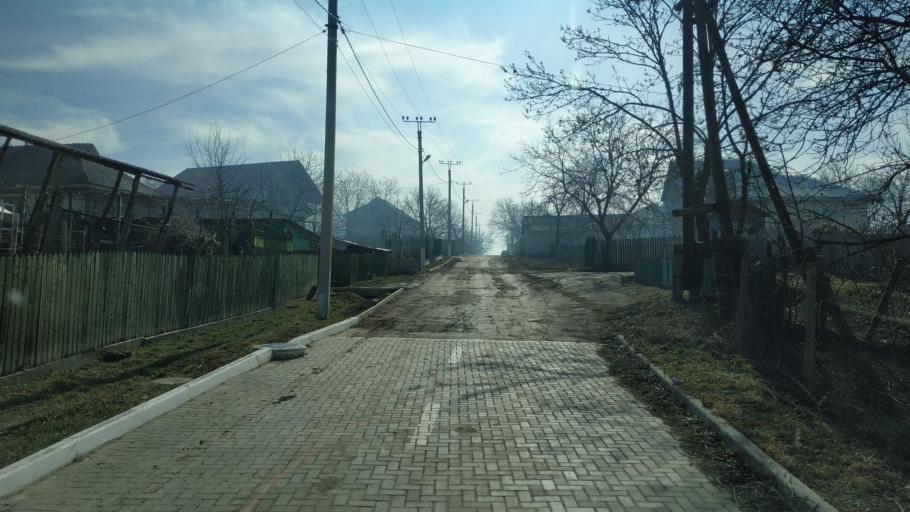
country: MD
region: Nisporeni
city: Nisporeni
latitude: 47.0753
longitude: 28.2639
